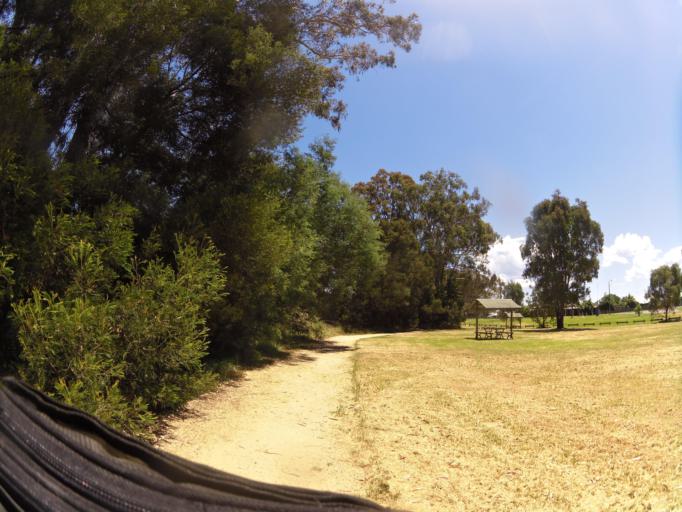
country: AU
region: Victoria
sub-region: Wellington
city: Sale
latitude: -37.9663
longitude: 146.9708
